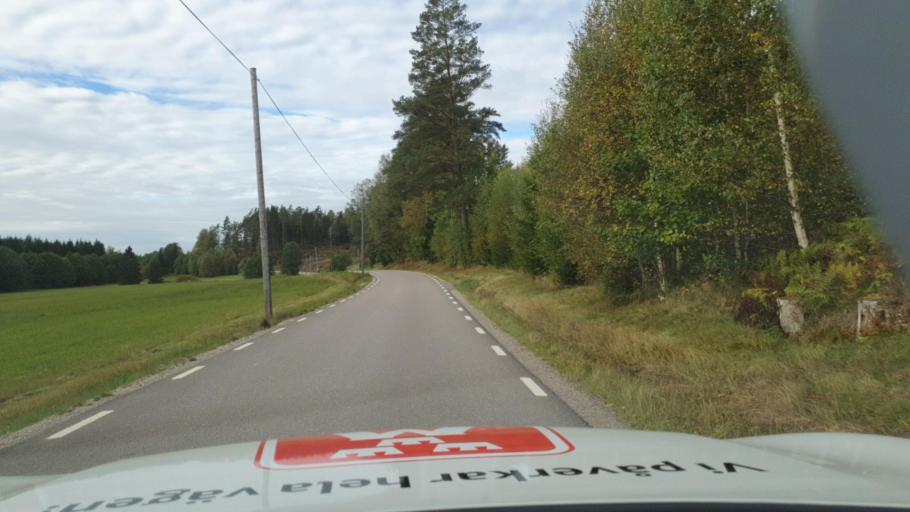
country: SE
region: Vaestra Goetaland
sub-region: Uddevalla Kommun
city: Uddevalla
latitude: 58.3943
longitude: 12.0941
